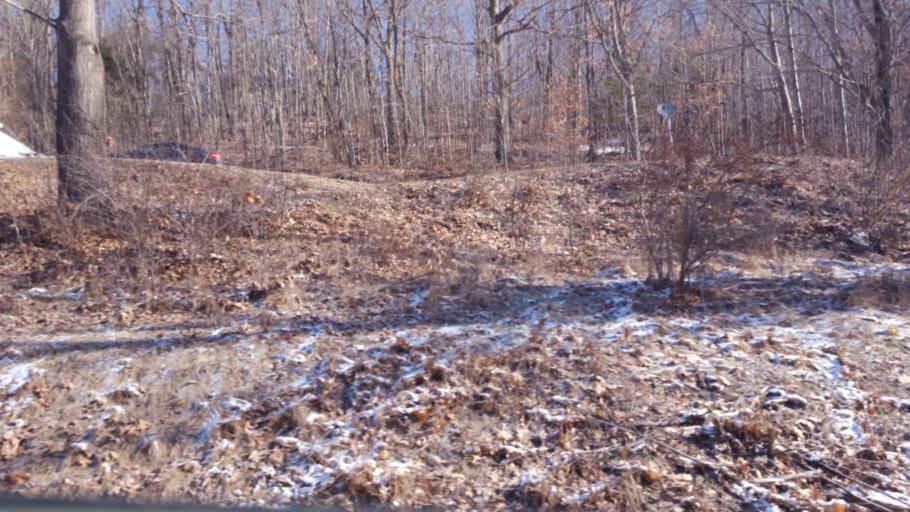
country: US
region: New York
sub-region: Allegany County
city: Wellsville
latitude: 42.1218
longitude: -77.9417
